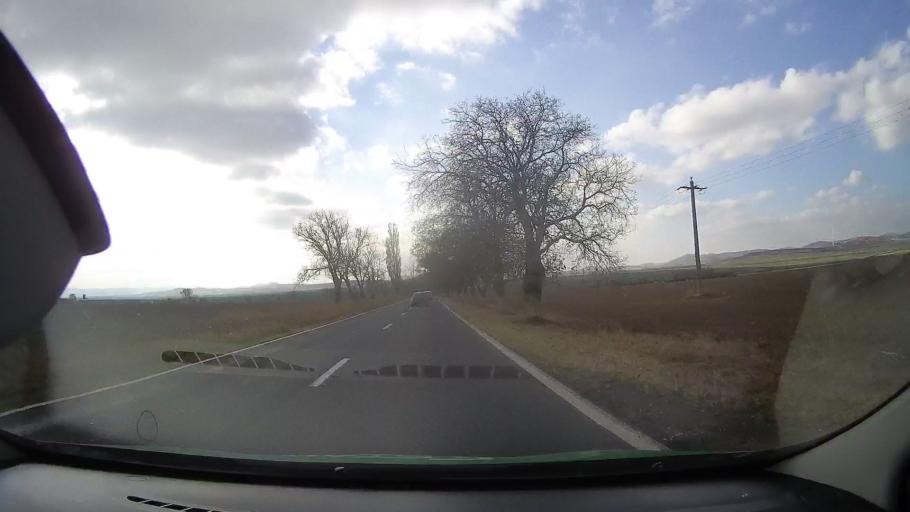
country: RO
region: Tulcea
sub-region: Comuna Frecatei
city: Frecatei
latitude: 45.0677
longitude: 28.6504
